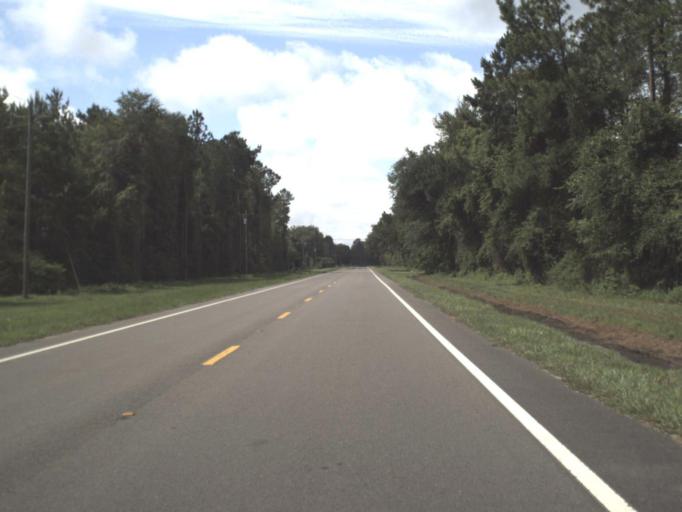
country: US
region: Florida
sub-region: Columbia County
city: Five Points
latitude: 30.2873
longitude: -82.6307
